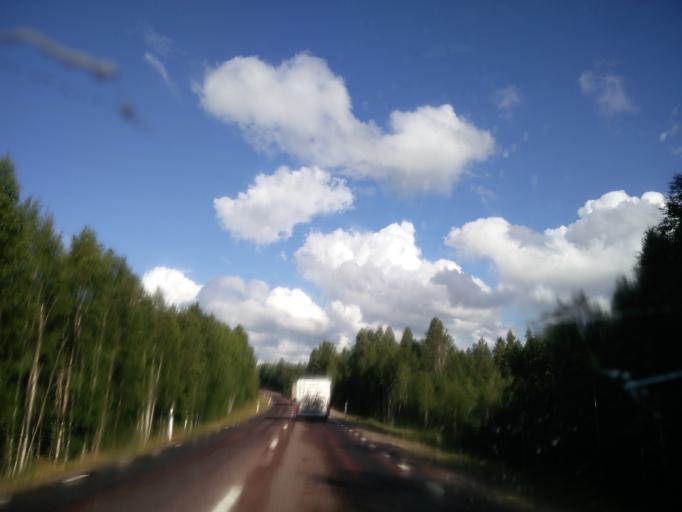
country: SE
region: Vaermland
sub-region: Hagfors Kommun
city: Ekshaerad
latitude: 60.4795
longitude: 13.3256
